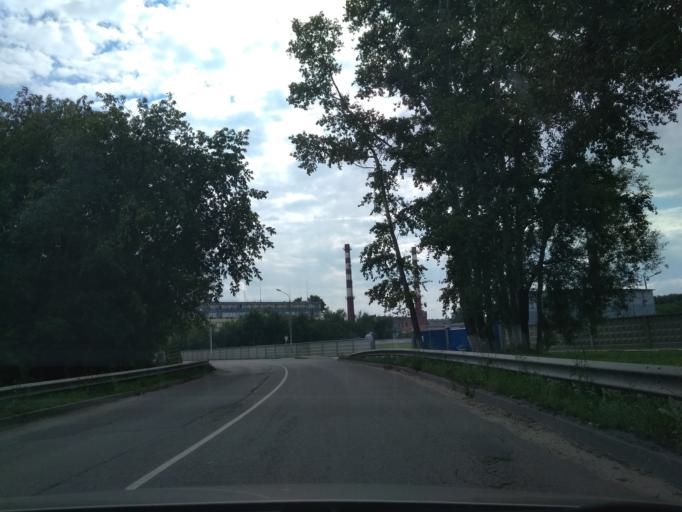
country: RU
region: Moskovskaya
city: Orekhovo-Zuyevo
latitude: 55.8009
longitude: 38.9493
